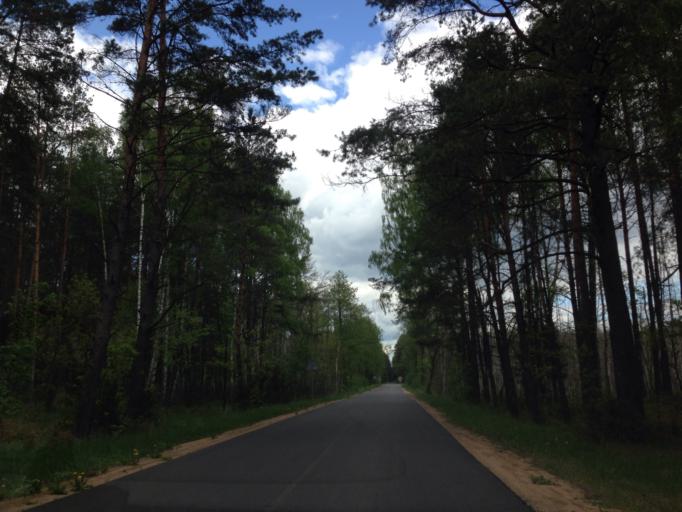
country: PL
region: Podlasie
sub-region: Powiat moniecki
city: Goniadz
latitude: 53.3494
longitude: 22.5975
